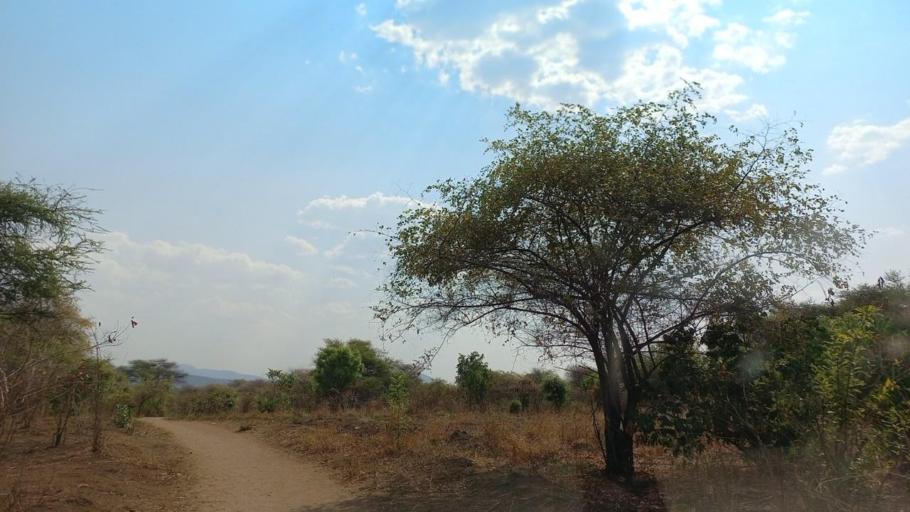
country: ZM
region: Lusaka
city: Luangwa
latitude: -15.0896
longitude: 30.1547
